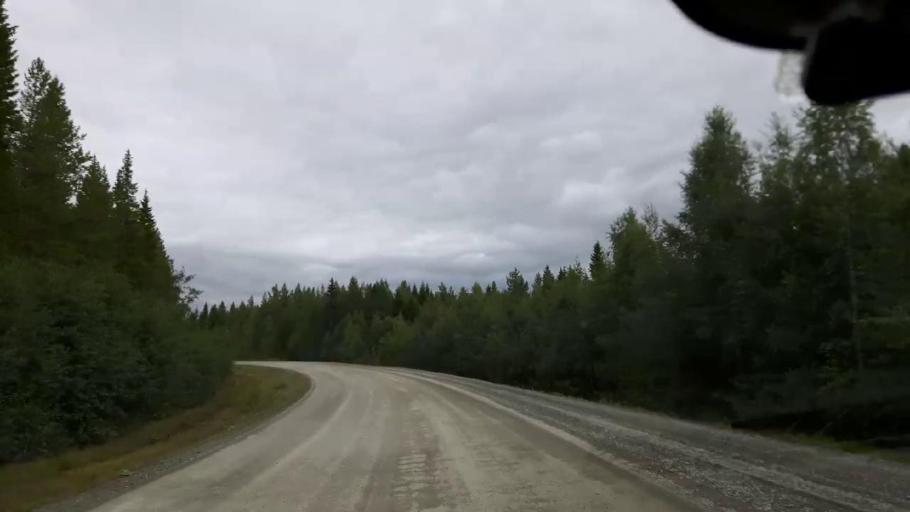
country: SE
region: Jaemtland
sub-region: OEstersunds Kommun
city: Brunflo
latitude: 63.1027
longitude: 15.0493
